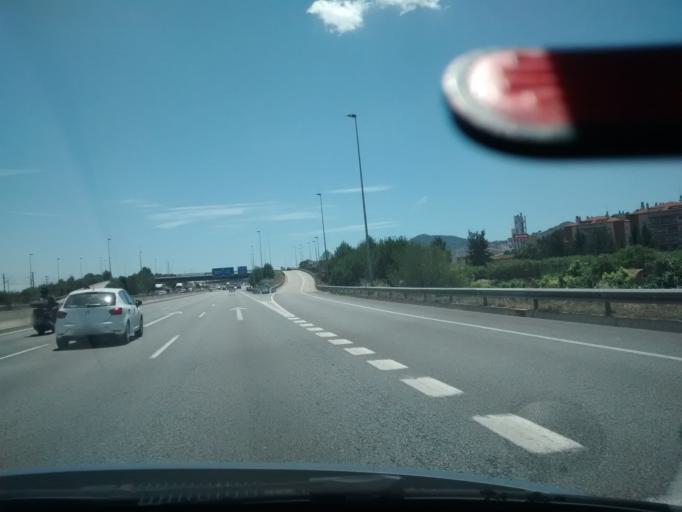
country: ES
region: Catalonia
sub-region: Provincia de Barcelona
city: Palleja
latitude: 41.4227
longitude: 2.0021
